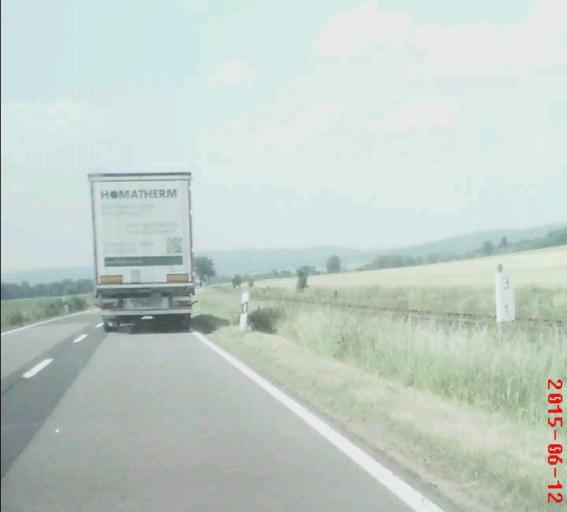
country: DE
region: Saxony-Anhalt
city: Uftrungen
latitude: 51.4746
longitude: 10.9898
